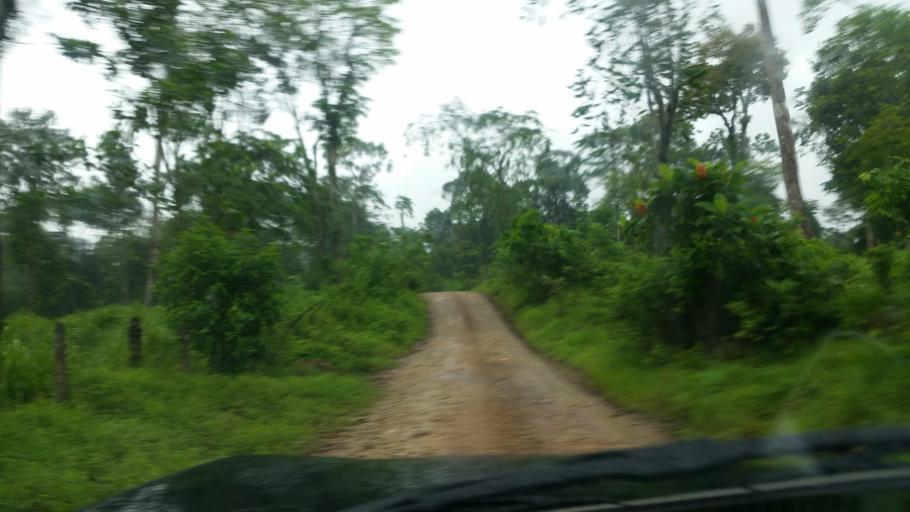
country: NI
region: Atlantico Norte (RAAN)
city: Bonanza
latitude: 14.0803
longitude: -84.6706
